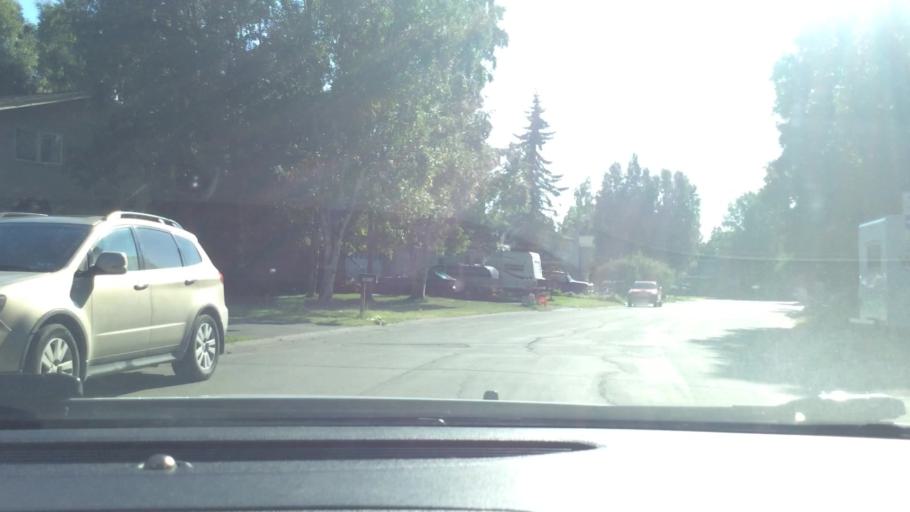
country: US
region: Alaska
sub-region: Anchorage Municipality
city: Elmendorf Air Force Base
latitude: 61.1833
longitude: -149.7302
